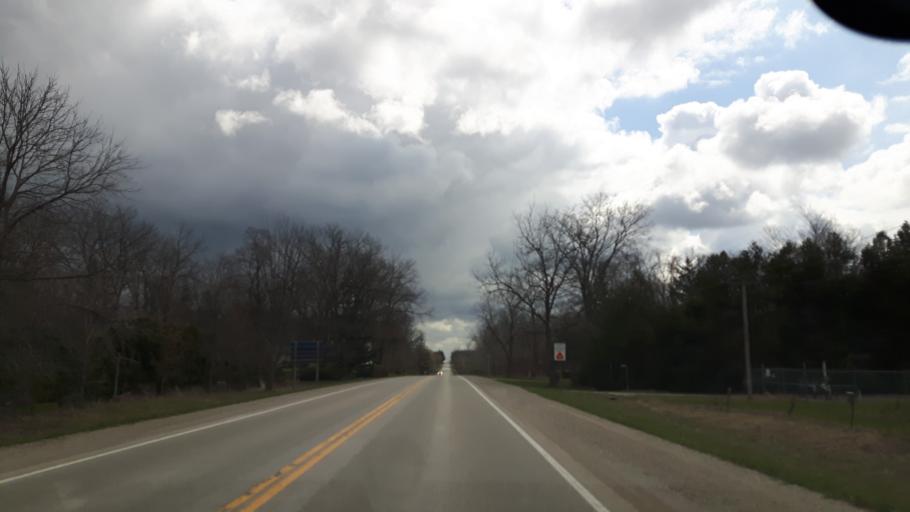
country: CA
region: Ontario
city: Bluewater
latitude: 43.5554
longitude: -81.6851
